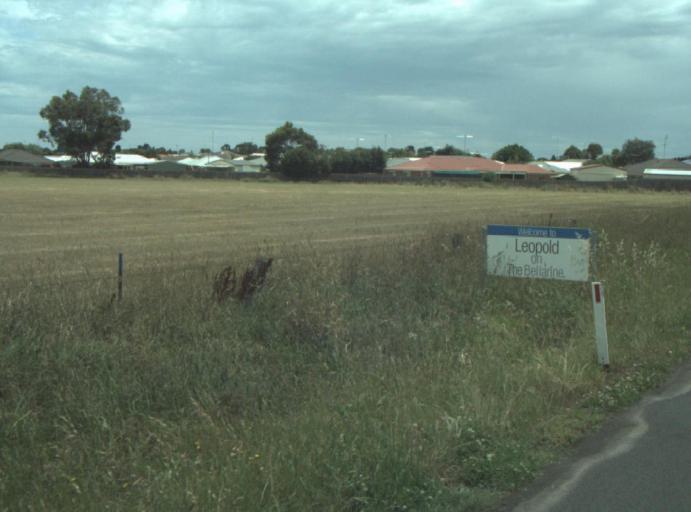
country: AU
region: Victoria
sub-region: Greater Geelong
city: Leopold
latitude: -38.1924
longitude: 144.4769
